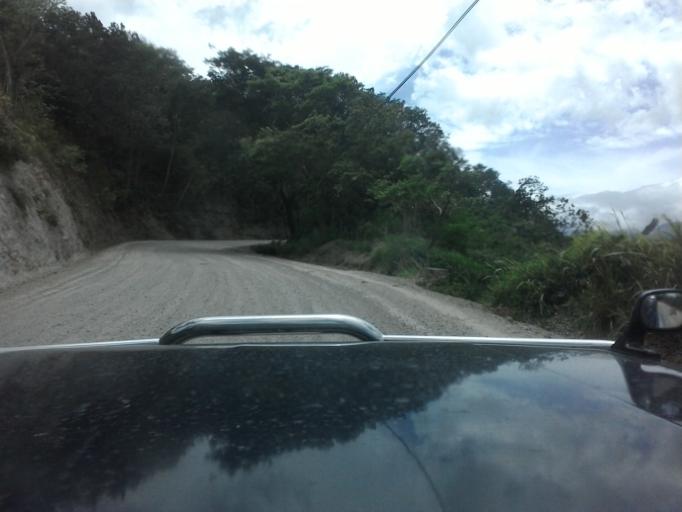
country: CR
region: Guanacaste
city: Juntas
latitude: 10.2238
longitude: -84.8502
